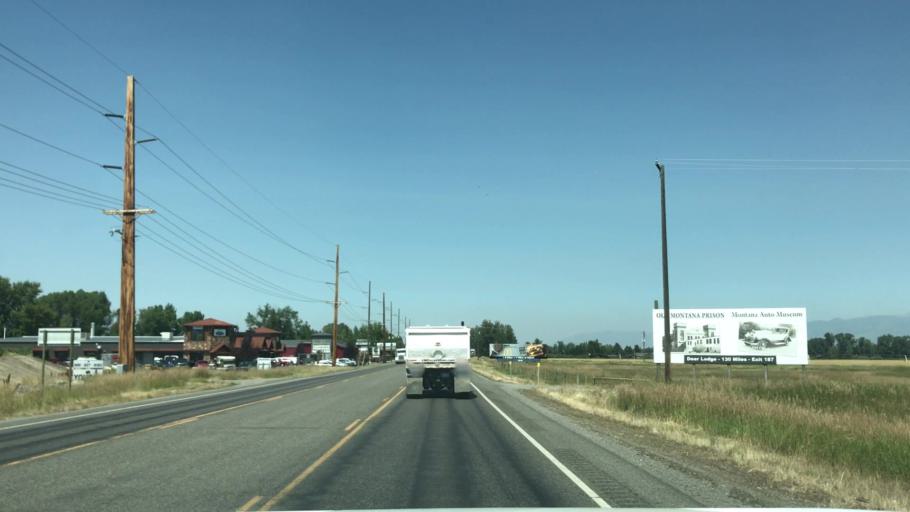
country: US
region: Montana
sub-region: Gallatin County
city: Four Corners
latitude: 45.6604
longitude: -111.1858
